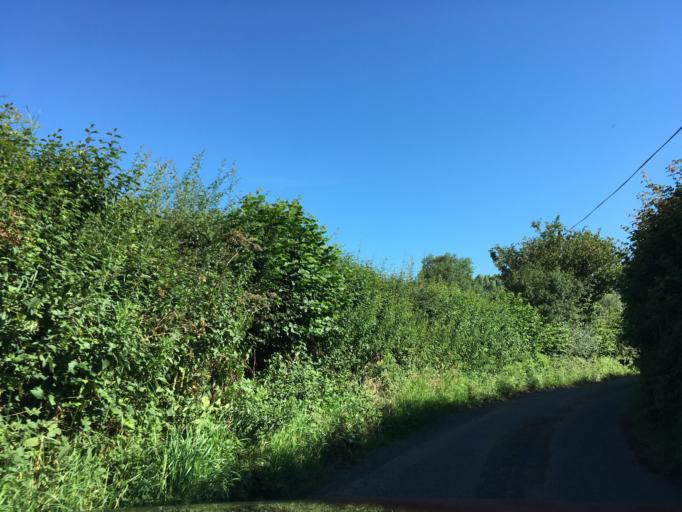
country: GB
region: England
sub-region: Herefordshire
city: Brockhampton
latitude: 51.9516
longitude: -2.5775
